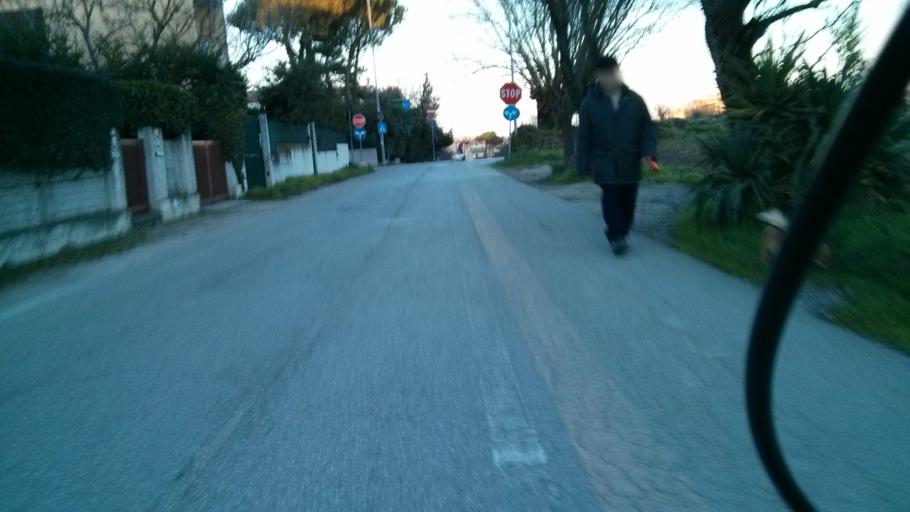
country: IT
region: The Marches
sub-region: Provincia di Pesaro e Urbino
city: Fano
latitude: 43.8454
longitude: 13.0072
